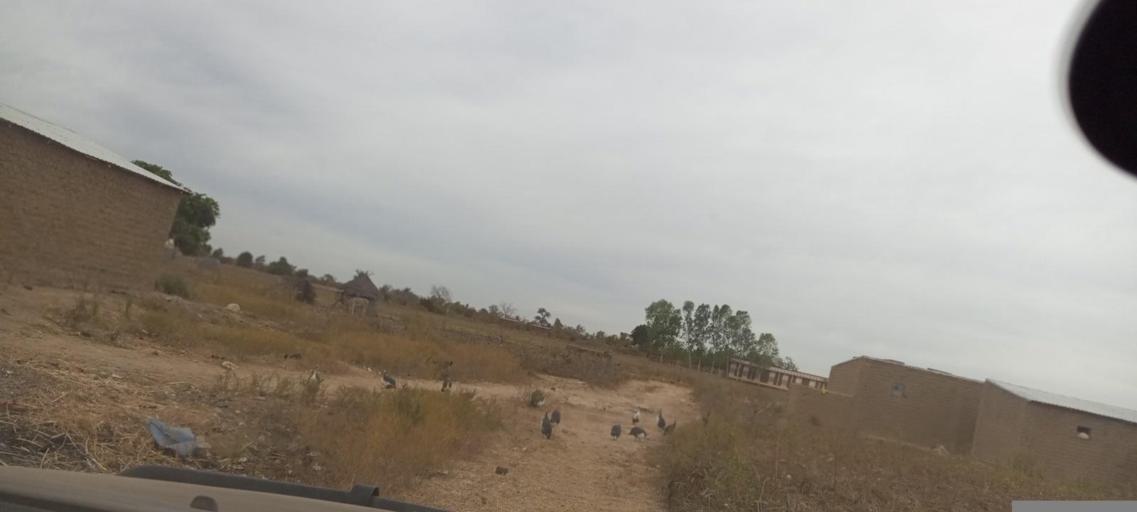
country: ML
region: Koulikoro
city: Kati
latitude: 12.7483
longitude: -8.3601
